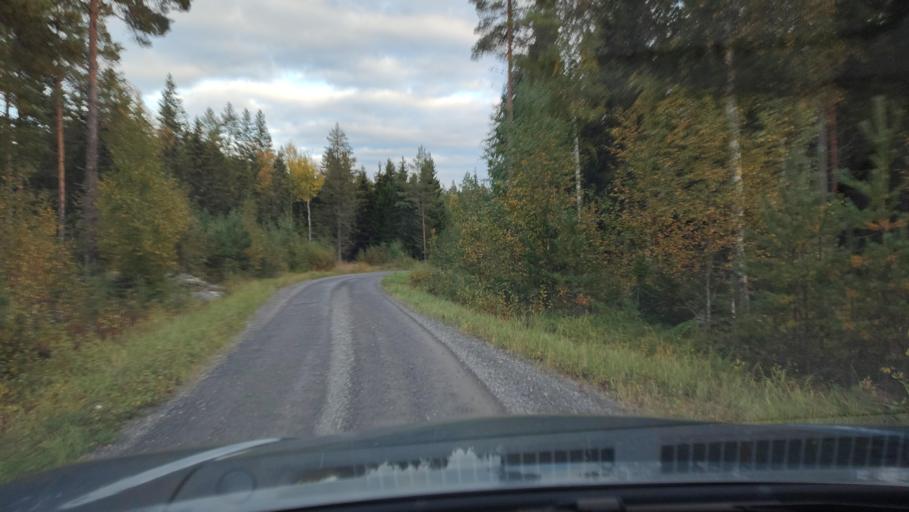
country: FI
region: Ostrobothnia
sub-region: Sydosterbotten
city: Kristinestad
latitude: 62.2305
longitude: 21.4195
